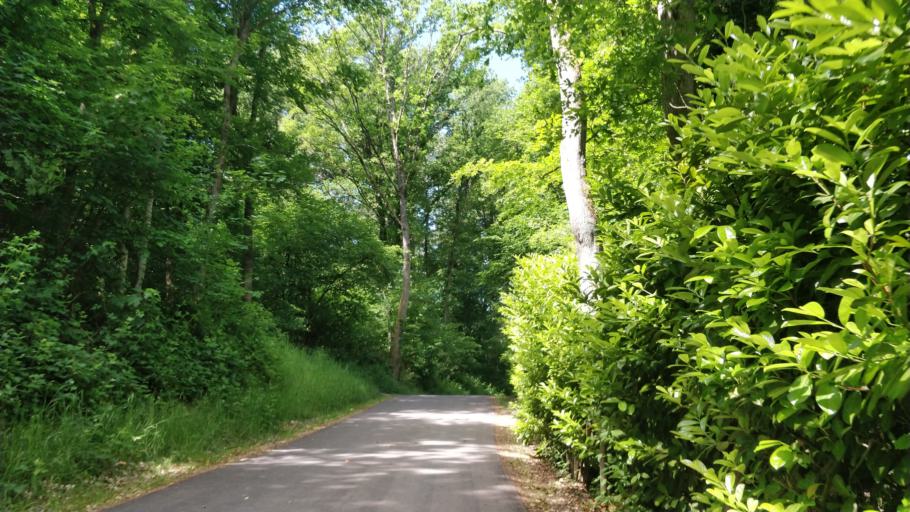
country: DE
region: Rheinland-Pfalz
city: Trier
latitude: 49.7377
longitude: 6.6587
